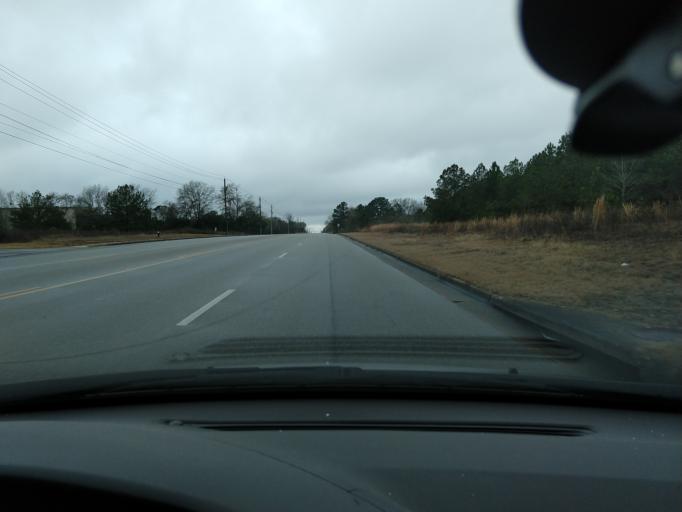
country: US
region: Alabama
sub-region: Houston County
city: Dothan
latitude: 31.2715
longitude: -85.3849
